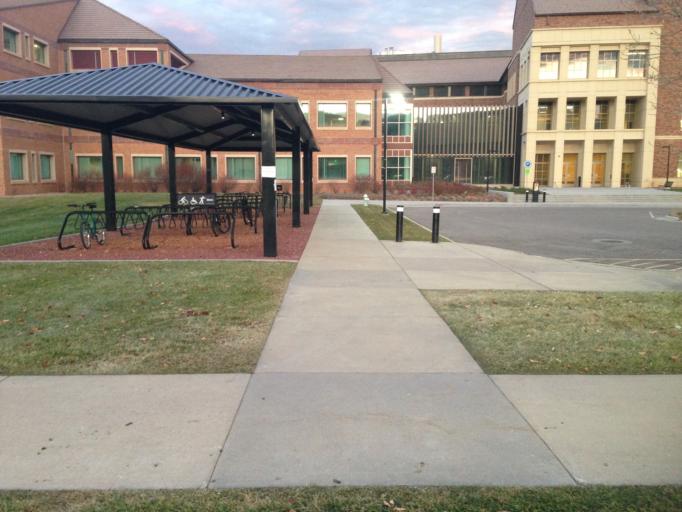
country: US
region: Colorado
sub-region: Boulder County
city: Boulder
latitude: 40.0089
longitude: -105.2427
